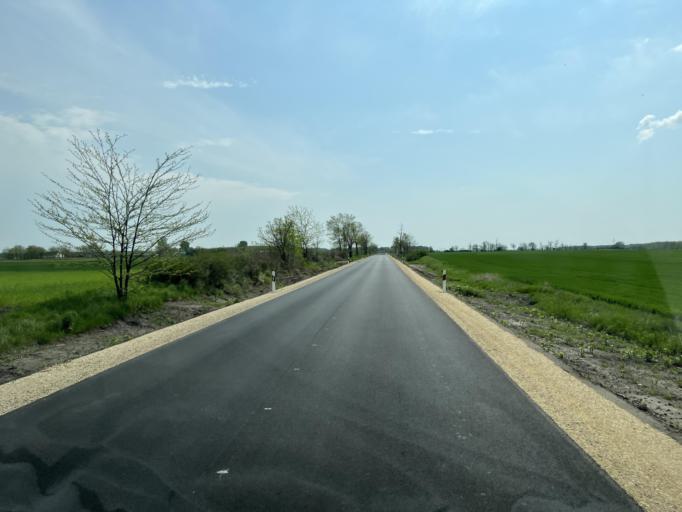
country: HU
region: Pest
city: Nagykoros
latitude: 47.0242
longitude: 19.8267
